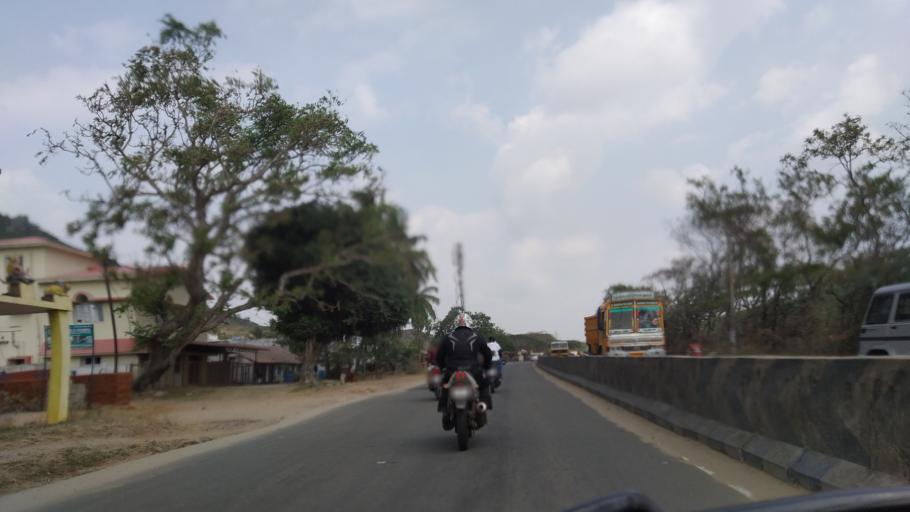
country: IN
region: Tamil Nadu
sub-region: Coimbatore
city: Madukkarai
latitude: 10.9161
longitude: 76.9484
